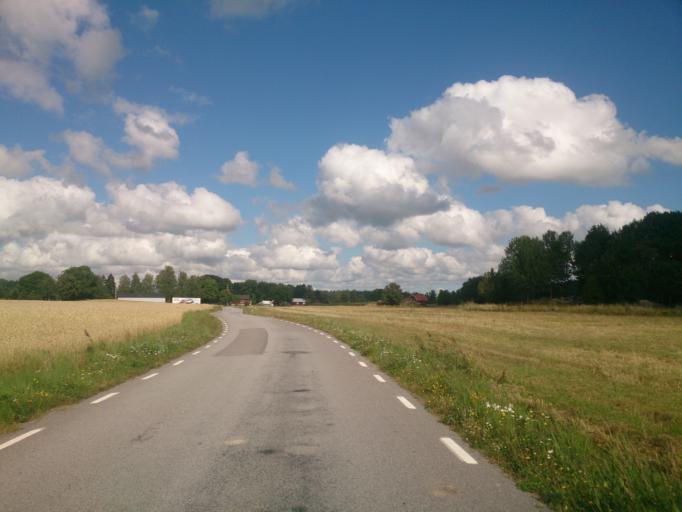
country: SE
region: OEstergoetland
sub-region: Atvidabergs Kommun
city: Atvidaberg
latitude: 58.3190
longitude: 15.9235
